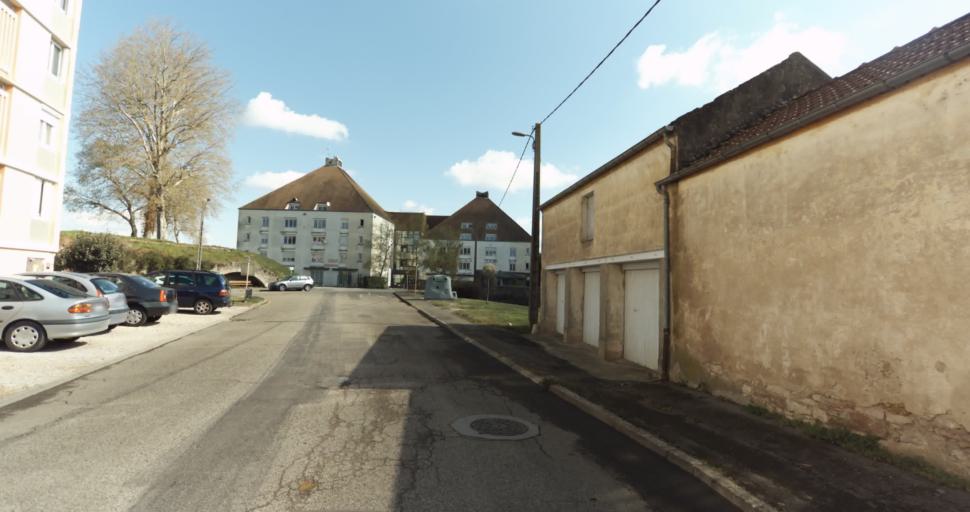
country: FR
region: Bourgogne
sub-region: Departement de la Cote-d'Or
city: Auxonne
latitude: 47.1958
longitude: 5.3859
